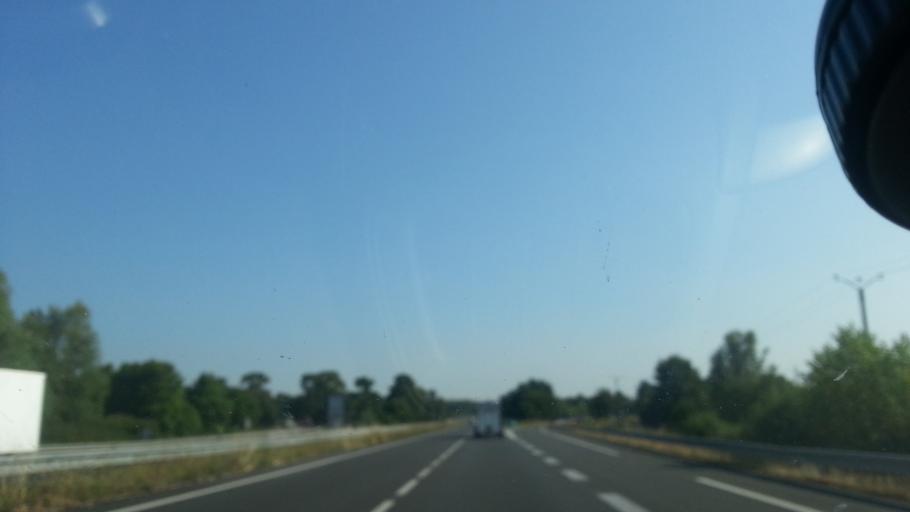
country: FR
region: Centre
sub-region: Departement d'Indre-et-Loire
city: La Celle-Saint-Avant
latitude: 47.0225
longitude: 0.5654
